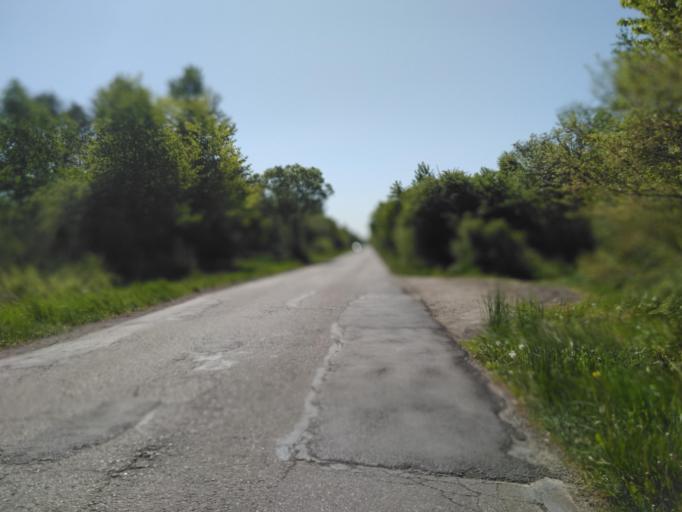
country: PL
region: Subcarpathian Voivodeship
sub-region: Krosno
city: Krosno
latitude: 49.6713
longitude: 21.7908
